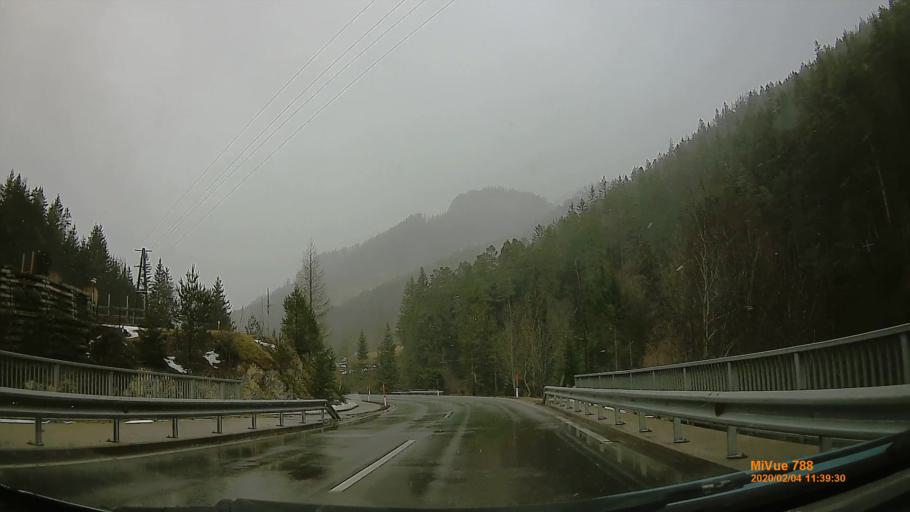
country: AT
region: Styria
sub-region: Politischer Bezirk Bruck-Muerzzuschlag
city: Muerzsteg
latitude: 47.6633
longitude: 15.5205
